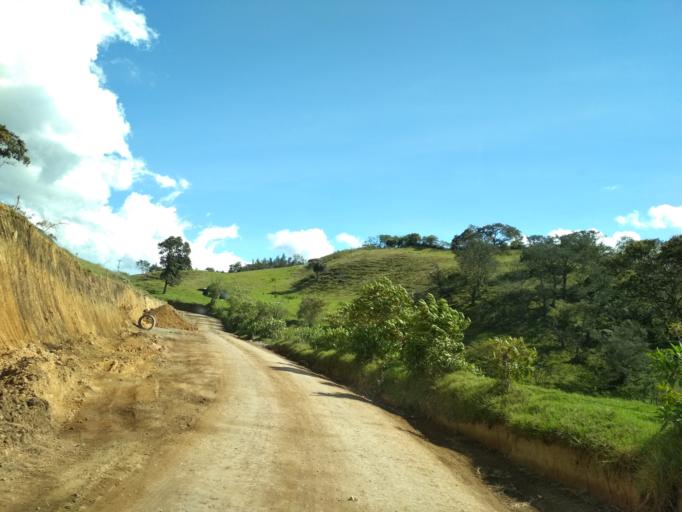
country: CO
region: Cauca
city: Jambalo
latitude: 2.7035
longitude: -76.3280
